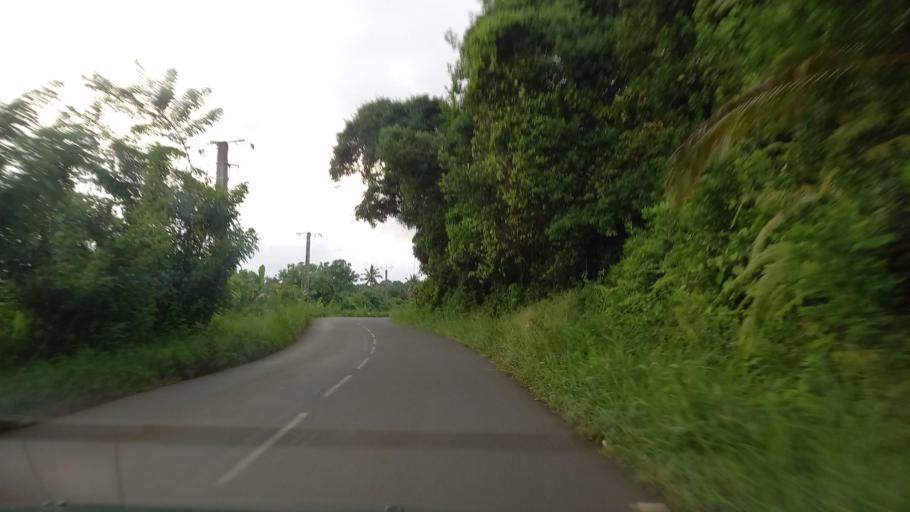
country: YT
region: M'Tsangamouji
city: M'Tsangamouji
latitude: -12.7629
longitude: 45.1009
